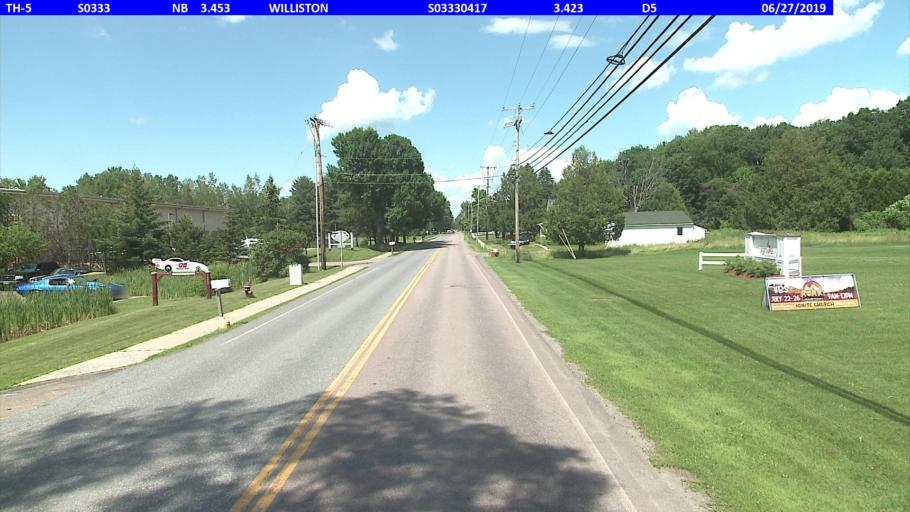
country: US
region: Vermont
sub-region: Chittenden County
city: Essex Junction
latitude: 44.4494
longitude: -73.1263
